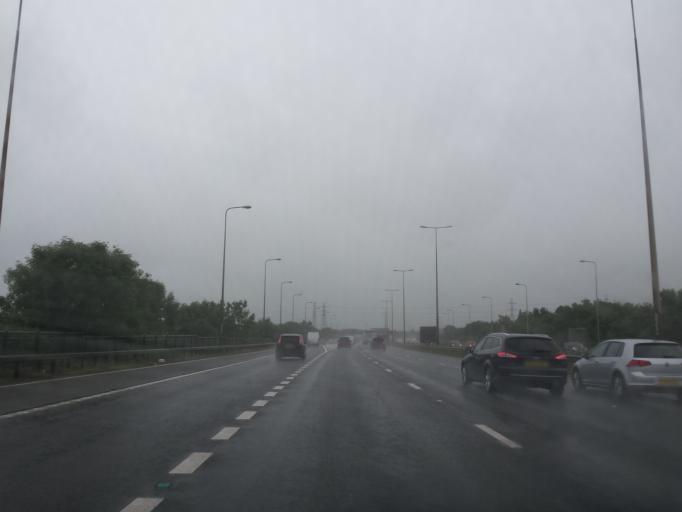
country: GB
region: England
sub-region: Leicestershire
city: Enderby
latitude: 52.6071
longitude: -1.1971
